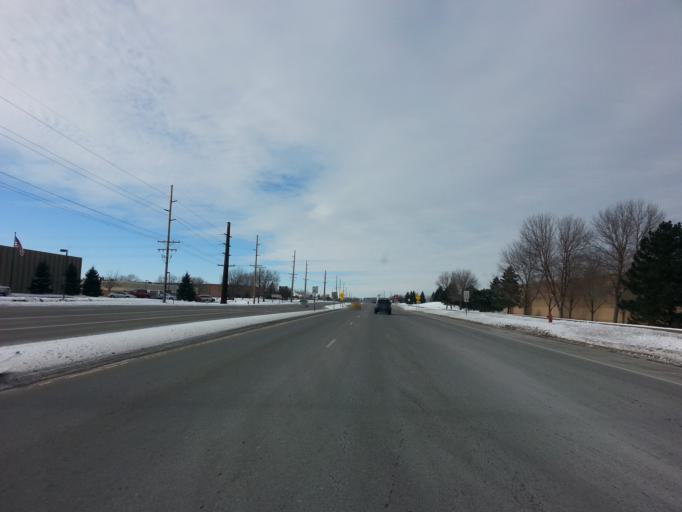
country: US
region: Minnesota
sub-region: Scott County
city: Savage
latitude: 44.7464
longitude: -93.3237
